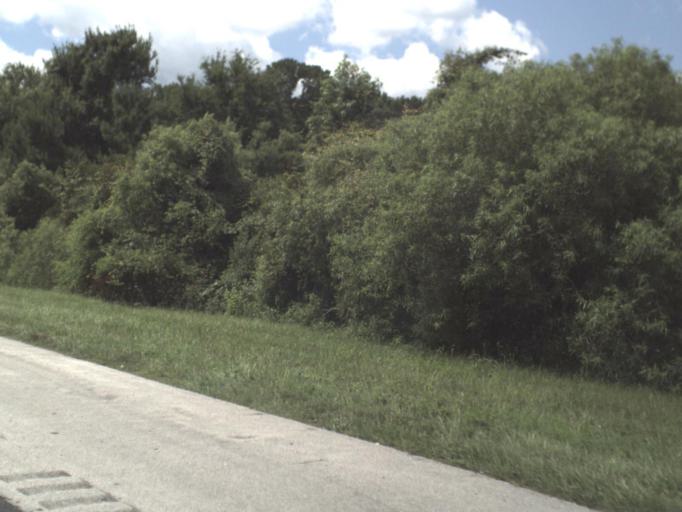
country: US
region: Florida
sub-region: Saint Johns County
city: Villano Beach
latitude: 29.9707
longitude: -81.4527
